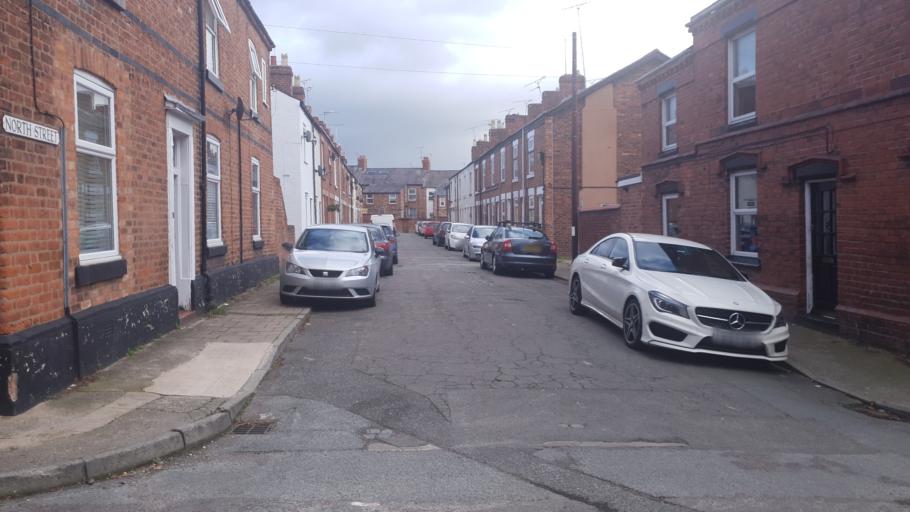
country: GB
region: England
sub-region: Cheshire West and Chester
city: Hoole
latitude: 53.1915
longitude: -2.8683
